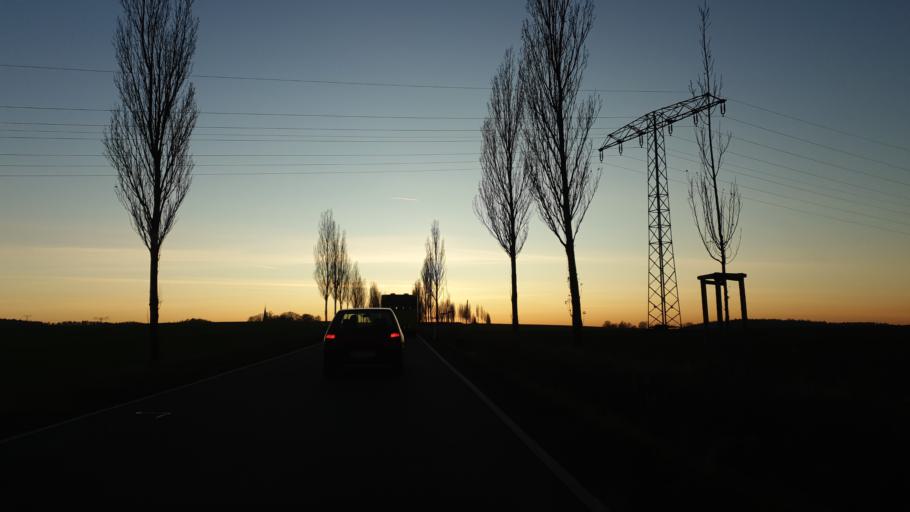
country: DE
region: Saxony
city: Hohndorf
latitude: 50.7525
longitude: 12.6827
